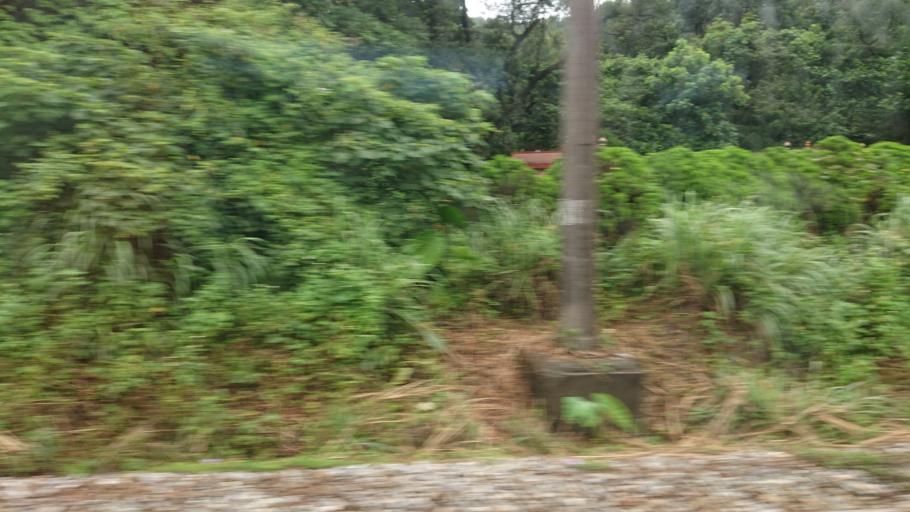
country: TW
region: Taiwan
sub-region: Keelung
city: Keelung
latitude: 25.0998
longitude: 121.8322
